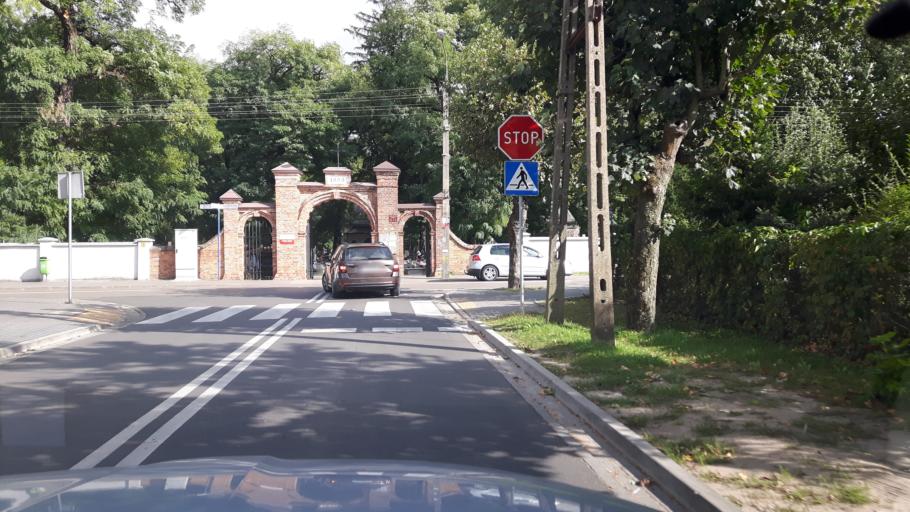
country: PL
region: Masovian Voivodeship
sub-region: Powiat wolominski
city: Kobylka
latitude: 52.3375
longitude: 21.2037
